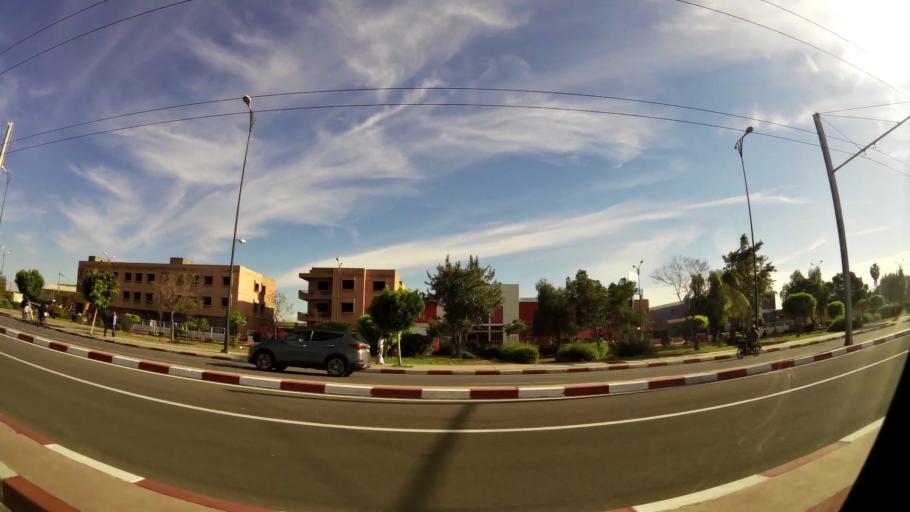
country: MA
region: Marrakech-Tensift-Al Haouz
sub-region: Marrakech
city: Marrakesh
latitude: 31.6278
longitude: -8.0476
